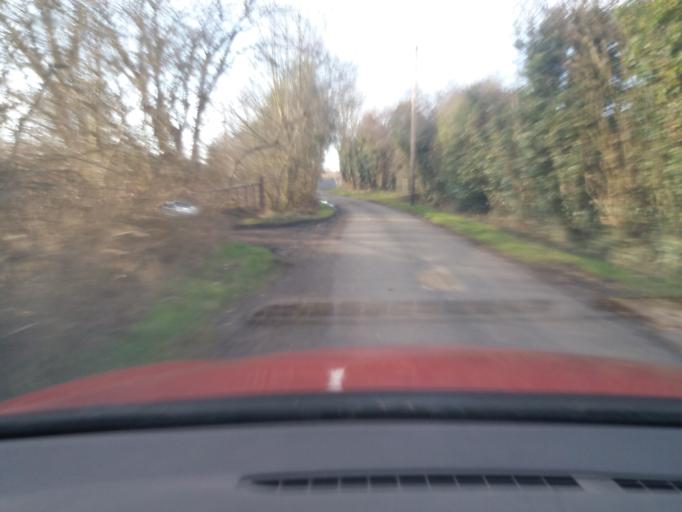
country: GB
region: England
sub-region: Lancashire
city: Euxton
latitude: 53.6510
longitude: -2.6684
